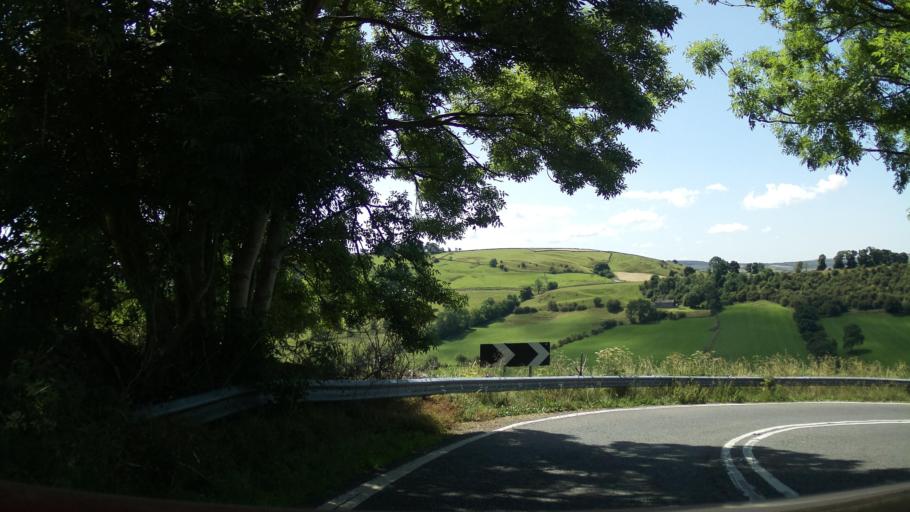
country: GB
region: England
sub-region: Derbyshire
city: Buxton
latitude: 53.1829
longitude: -1.8471
